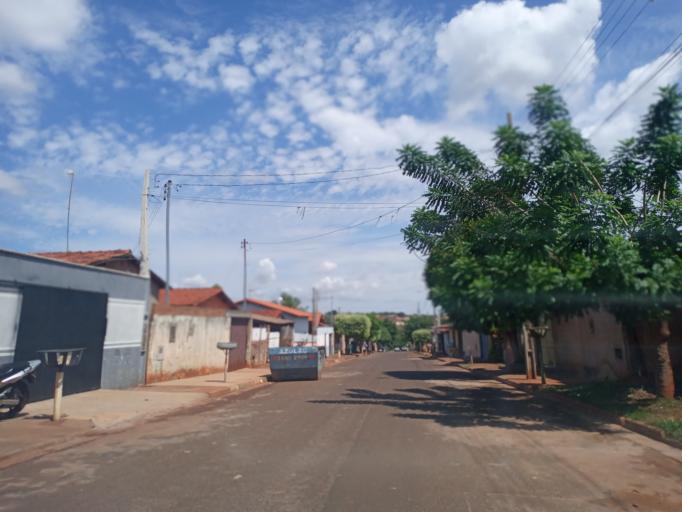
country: BR
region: Minas Gerais
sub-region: Ituiutaba
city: Ituiutaba
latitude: -18.9987
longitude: -49.4750
